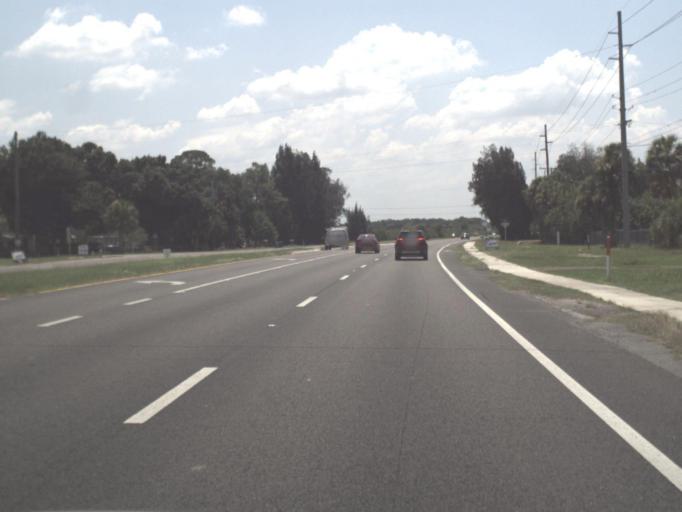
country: US
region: Florida
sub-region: Hillsborough County
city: Gibsonton
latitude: 27.8229
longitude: -82.3821
